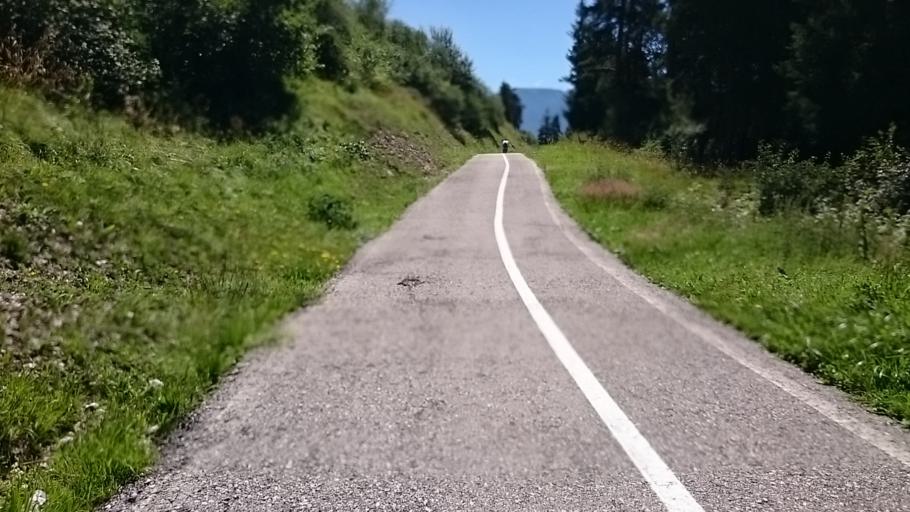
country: IT
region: Veneto
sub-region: Provincia di Belluno
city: San Vito
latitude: 46.4834
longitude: 12.1930
